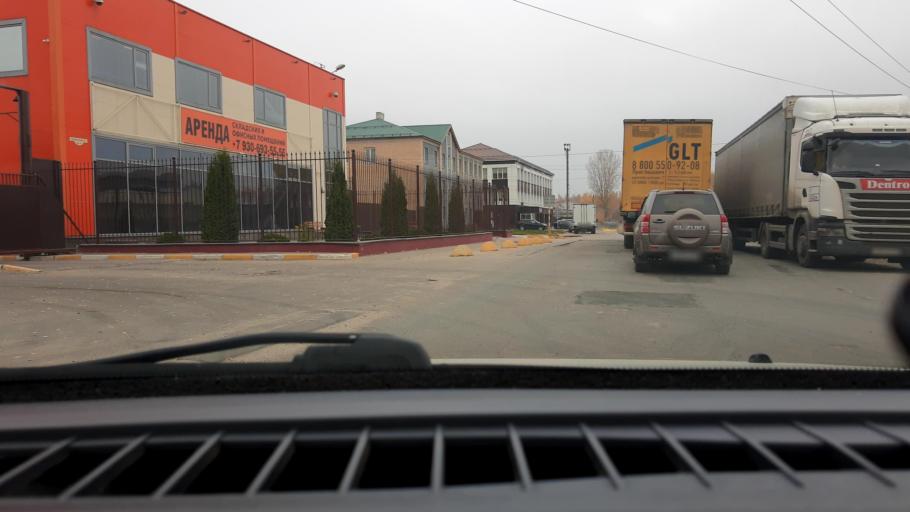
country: RU
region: Nizjnij Novgorod
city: Gorbatovka
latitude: 56.3534
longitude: 43.7947
